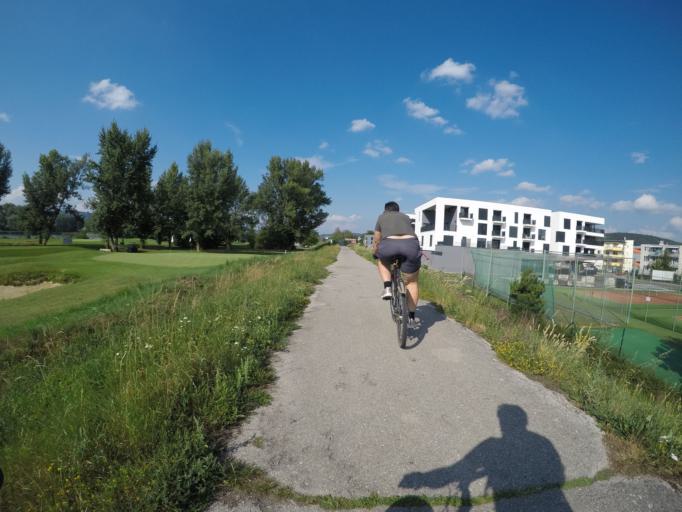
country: SK
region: Trenciansky
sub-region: Okres Trencin
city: Trencin
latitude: 48.8843
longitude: 18.0222
